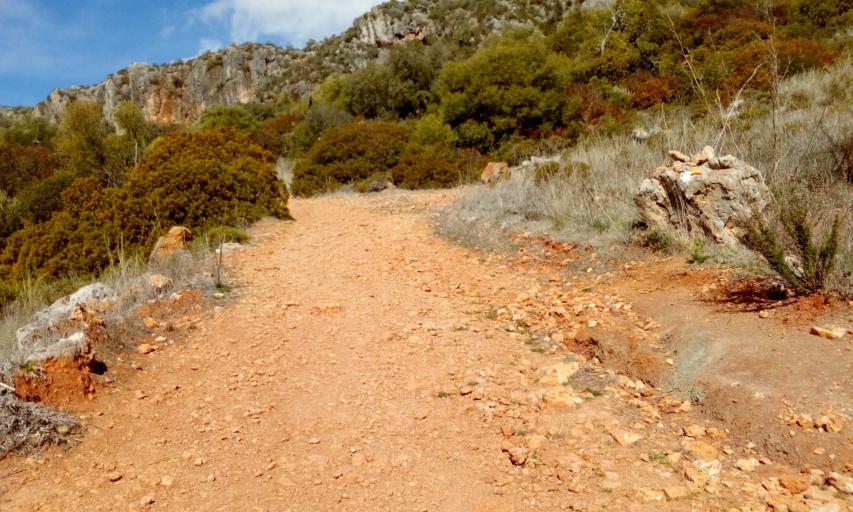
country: PT
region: Faro
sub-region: Loule
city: Boliqueime
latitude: 37.2521
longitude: -8.0992
